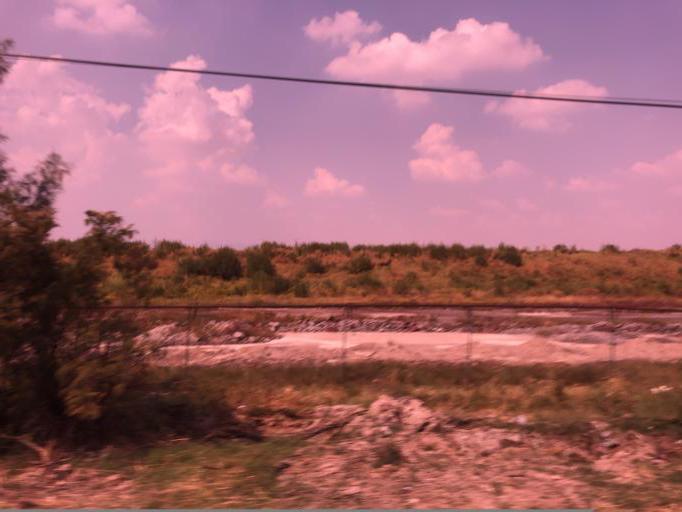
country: MX
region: Mexico
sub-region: Ciudad Nezahualcoyotl
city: Colonia Gustavo Baz Prada
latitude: 19.4656
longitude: -99.0153
